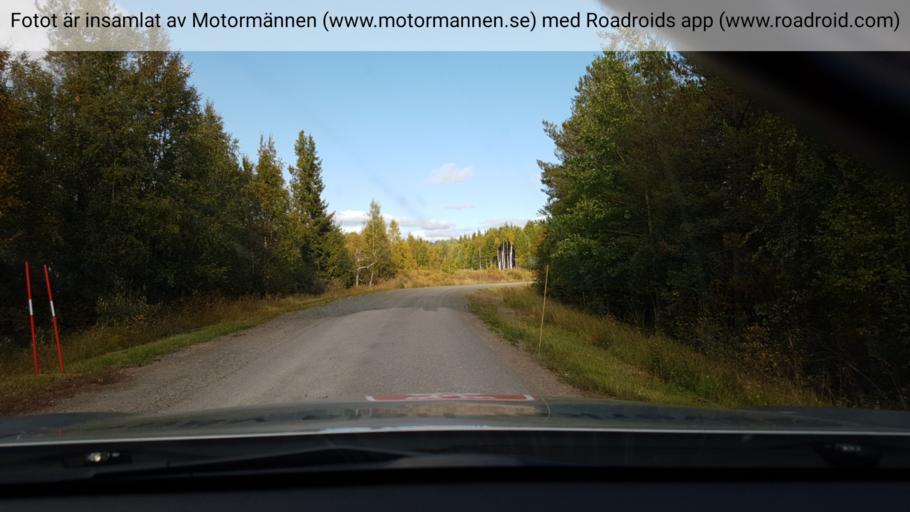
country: SE
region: Vaesterbotten
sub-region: Sorsele Kommun
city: Sorsele
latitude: 65.4630
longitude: 17.7581
